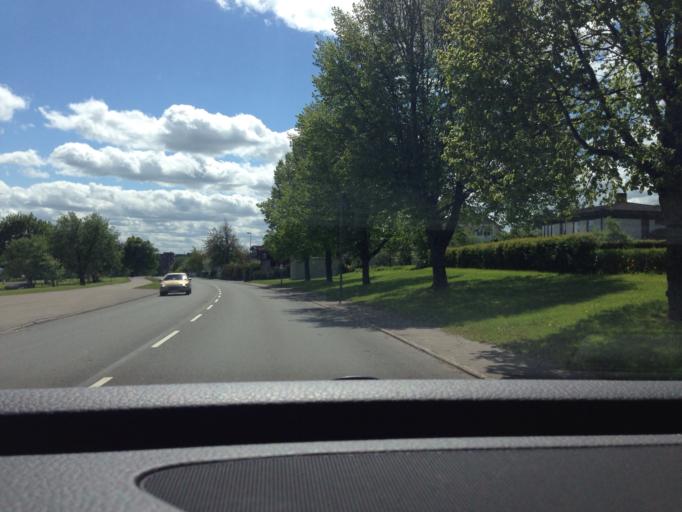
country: SE
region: Vaestra Goetaland
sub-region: Skovde Kommun
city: Skoevde
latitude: 58.4066
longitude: 13.8325
